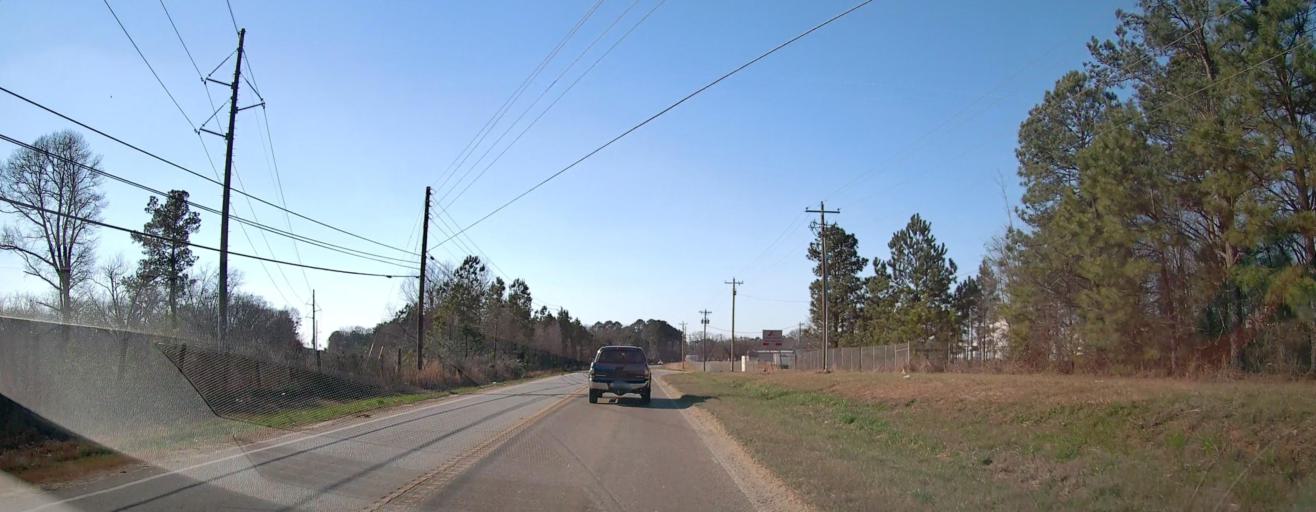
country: US
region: Georgia
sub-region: Butts County
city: Jackson
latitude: 33.2843
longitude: -83.9313
